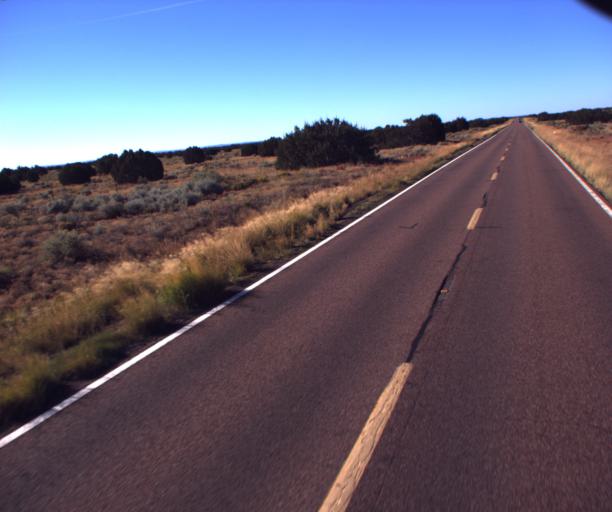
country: US
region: Arizona
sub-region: Navajo County
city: Heber-Overgaard
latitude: 34.5815
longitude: -110.4045
